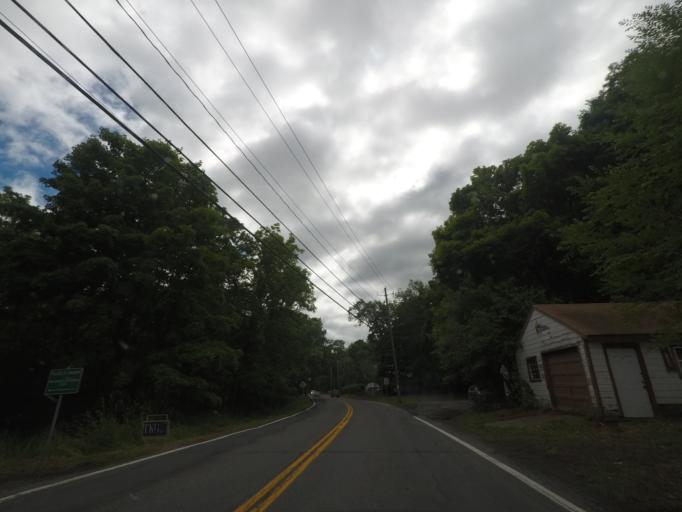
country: US
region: New York
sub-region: Columbia County
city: Philmont
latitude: 42.2524
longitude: -73.6682
